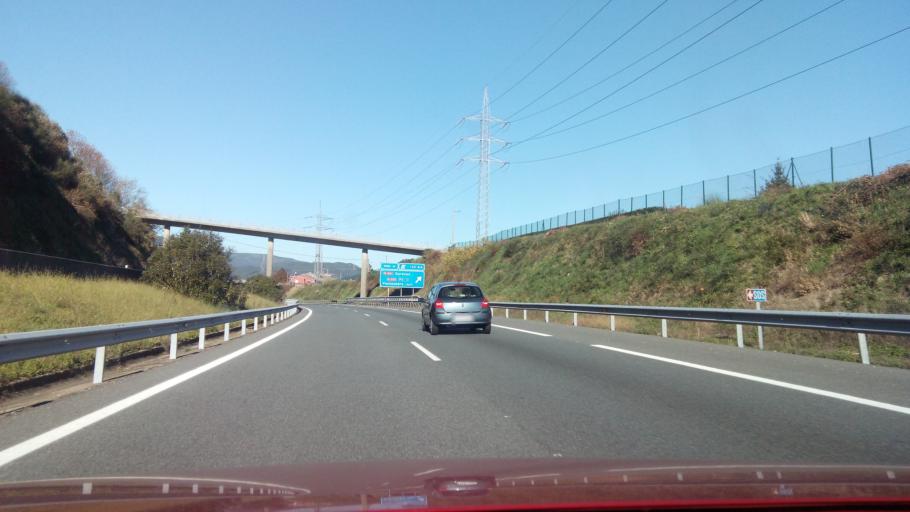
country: ES
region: Galicia
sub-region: Provincia de Pontevedra
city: Pontevedra
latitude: 42.4013
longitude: -8.6491
